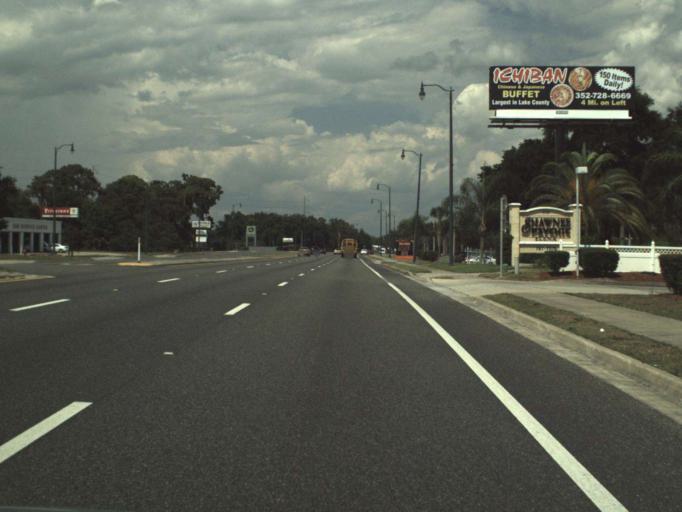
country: US
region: Florida
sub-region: Lake County
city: Leesburg
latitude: 28.8162
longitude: -81.8476
